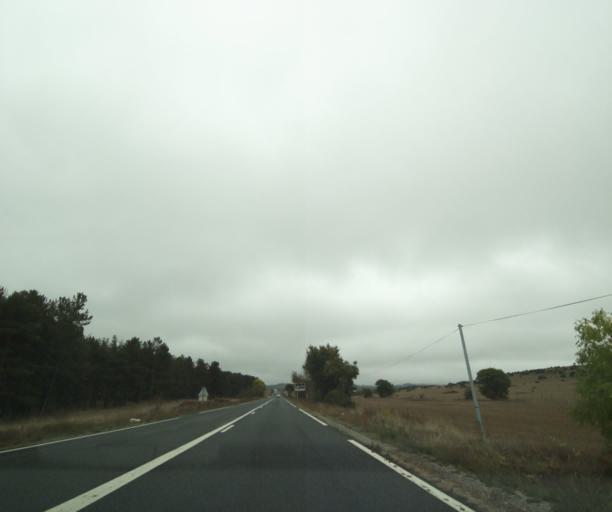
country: FR
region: Midi-Pyrenees
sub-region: Departement de l'Aveyron
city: La Cavalerie
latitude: 44.0305
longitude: 3.1474
